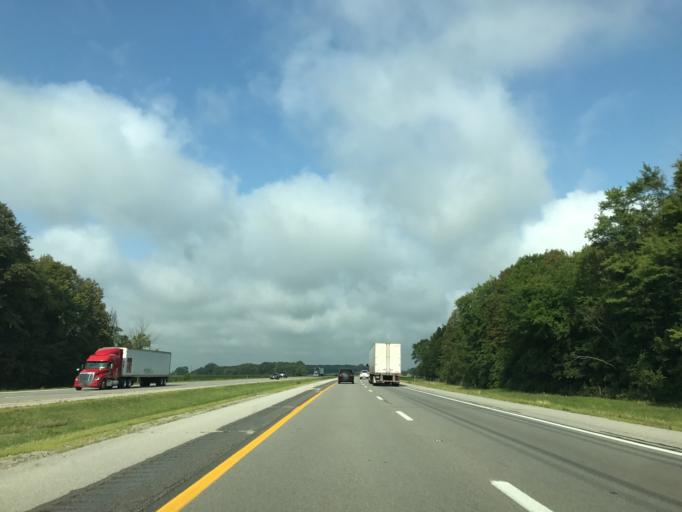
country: US
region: Ohio
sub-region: Williams County
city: West Unity
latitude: 41.6080
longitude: -84.5028
